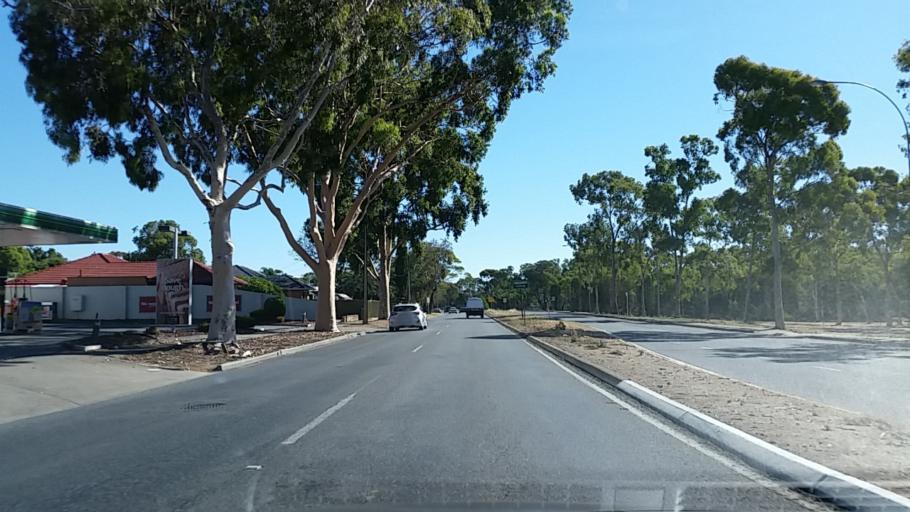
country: AU
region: South Australia
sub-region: Salisbury
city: Ingle Farm
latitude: -34.8136
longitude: 138.6432
